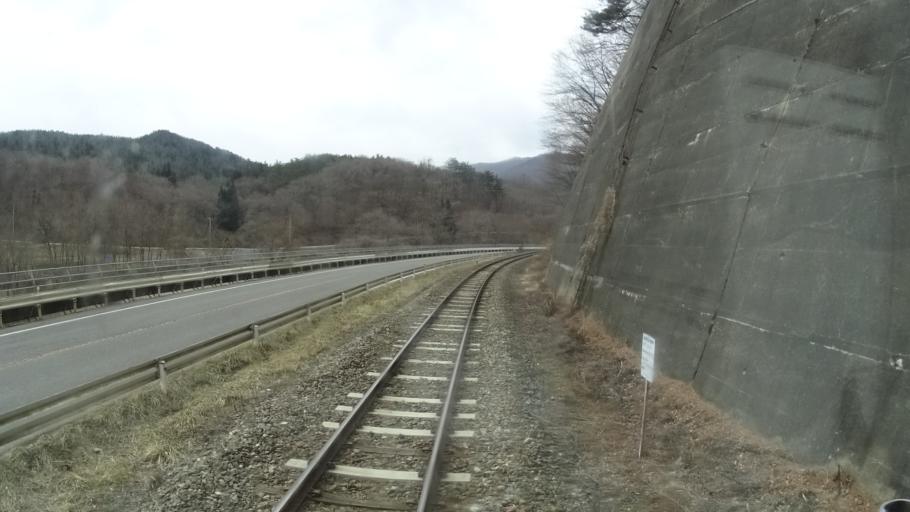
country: JP
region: Iwate
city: Tono
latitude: 39.3027
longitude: 141.3883
